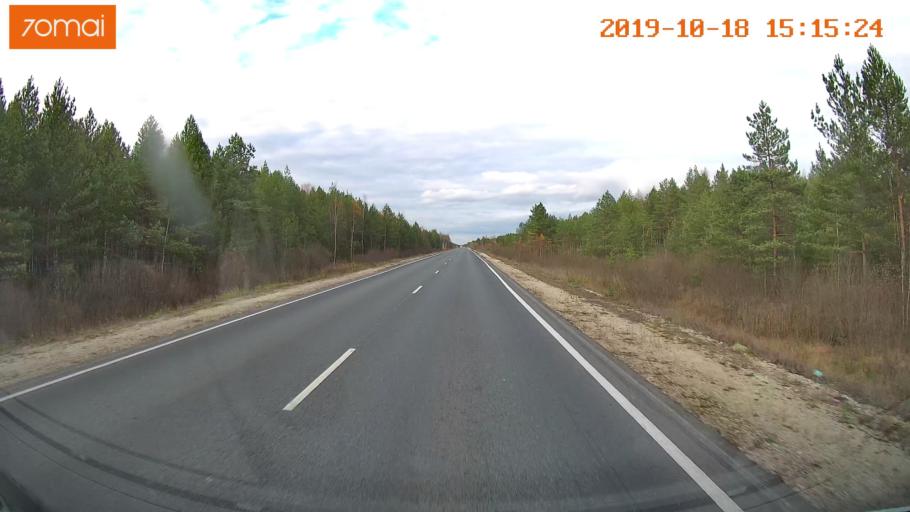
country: RU
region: Vladimir
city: Gus'-Khrustal'nyy
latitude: 55.6183
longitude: 40.7224
